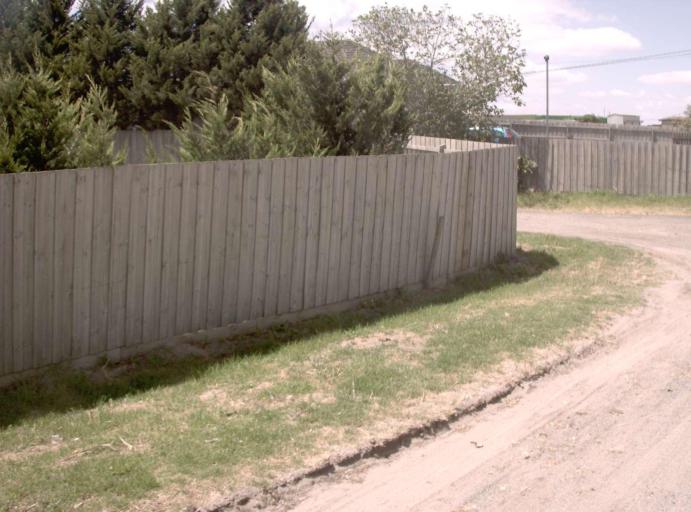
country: AU
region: Victoria
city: Heatherton
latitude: -37.9669
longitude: 145.1127
